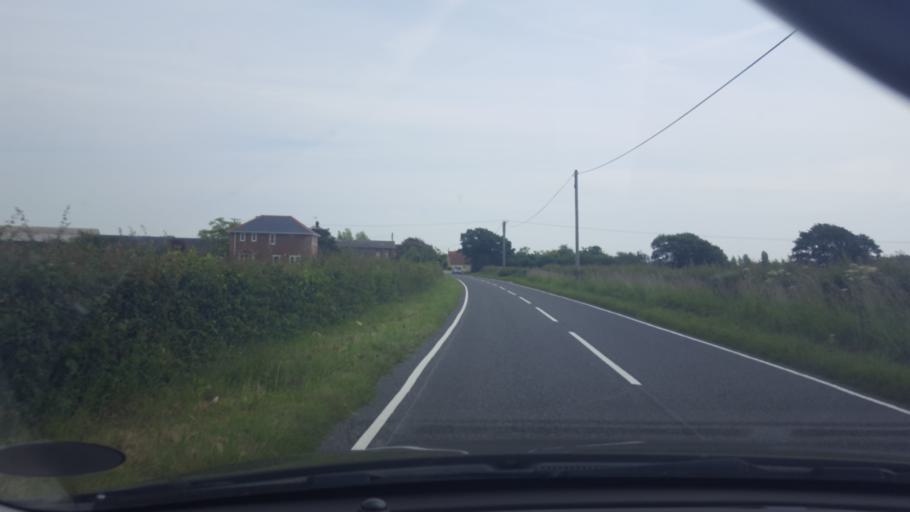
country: GB
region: England
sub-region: Essex
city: Little Clacton
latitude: 51.8262
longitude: 1.1560
